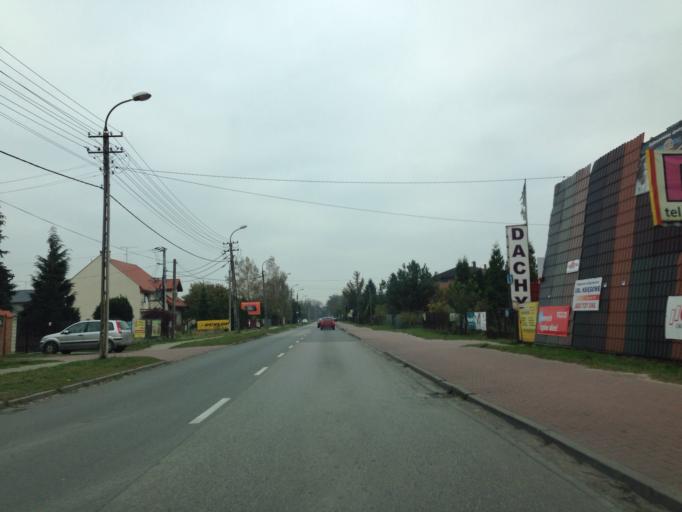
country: PL
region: Masovian Voivodeship
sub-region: Powiat warszawski zachodni
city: Stare Babice
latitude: 52.2530
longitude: 20.8070
